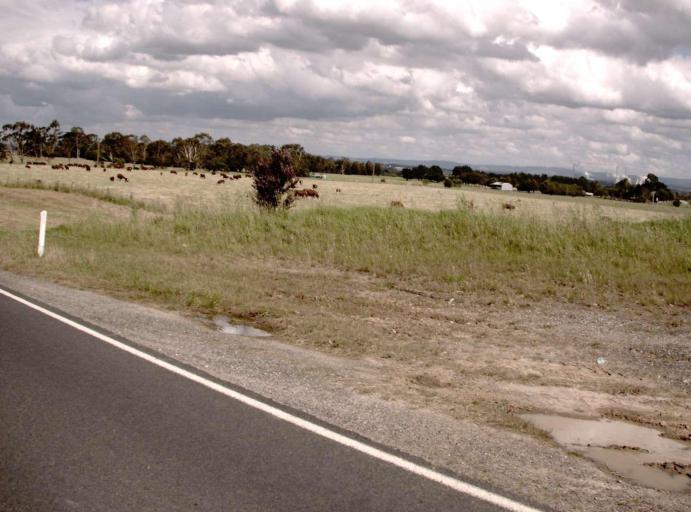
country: AU
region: Victoria
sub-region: Latrobe
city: Traralgon
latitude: -38.1537
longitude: 146.5172
